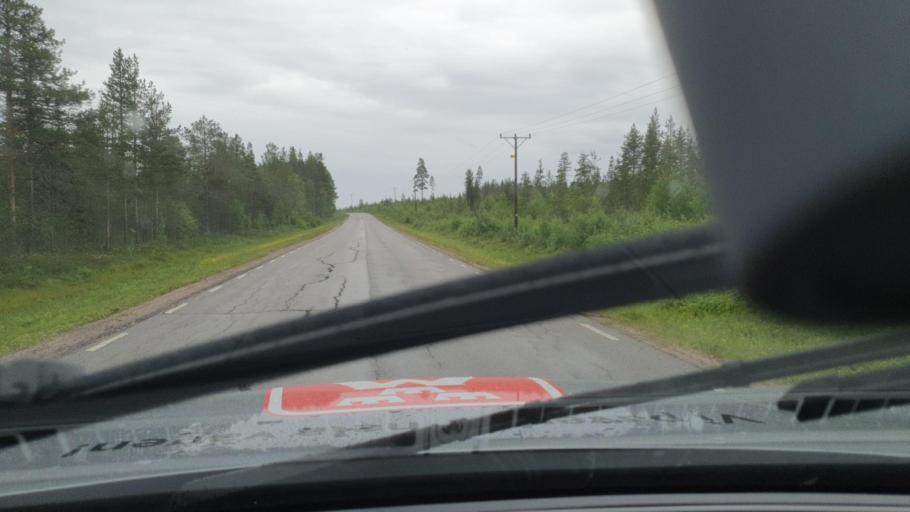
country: SE
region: Norrbotten
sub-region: Pajala Kommun
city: Pajala
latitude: 66.7905
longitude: 23.1265
